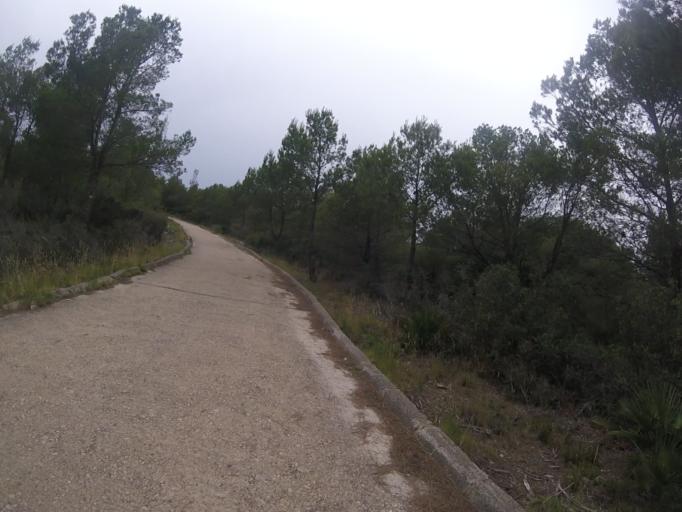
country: ES
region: Valencia
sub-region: Provincia de Castello
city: Alcoceber
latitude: 40.2822
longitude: 0.2832
